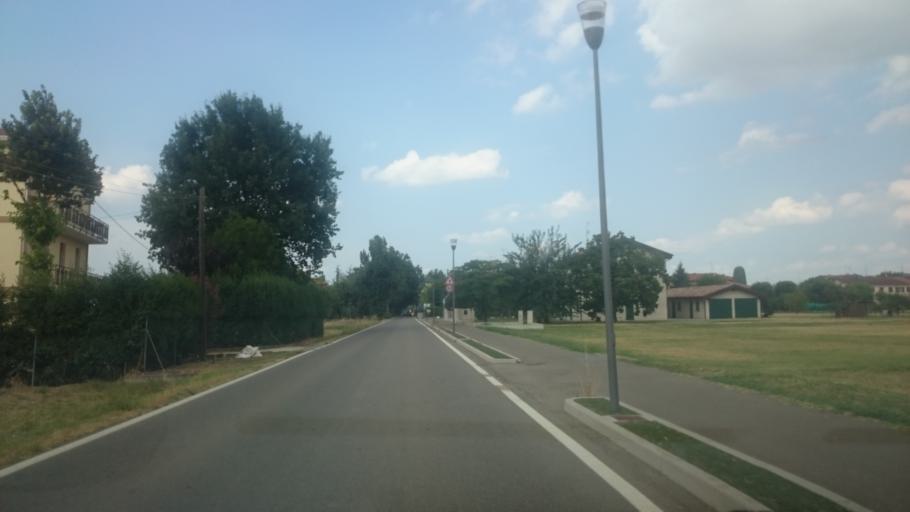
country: IT
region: Emilia-Romagna
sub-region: Provincia di Reggio Emilia
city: Salvaterra
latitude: 44.5935
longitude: 10.7598
